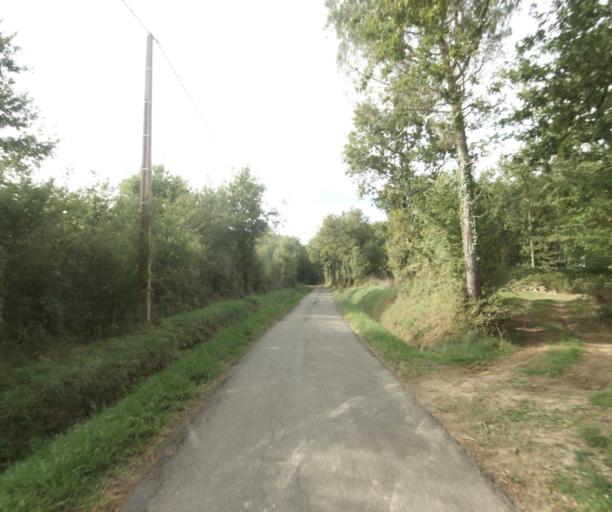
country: FR
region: Midi-Pyrenees
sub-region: Departement du Gers
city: Le Houga
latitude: 43.8612
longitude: -0.1347
